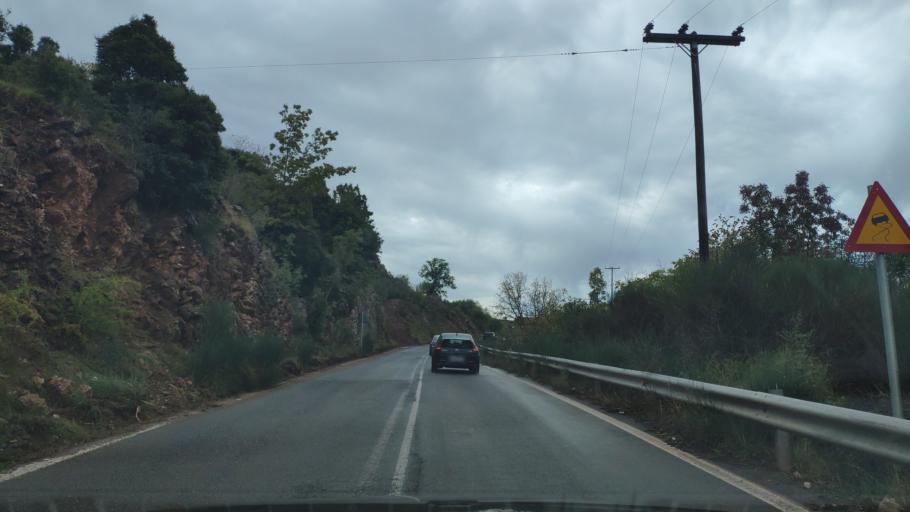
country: GR
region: Peloponnese
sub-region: Nomos Arkadias
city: Dimitsana
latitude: 37.6037
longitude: 22.0404
